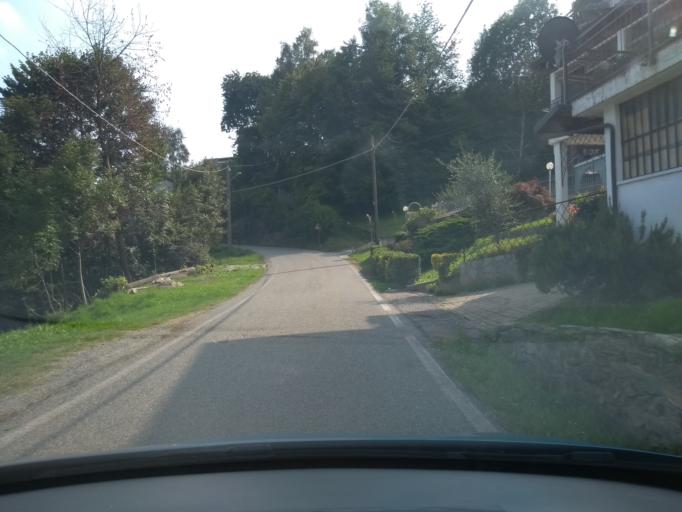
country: IT
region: Piedmont
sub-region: Provincia di Torino
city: Corio
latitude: 45.3133
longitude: 7.5198
